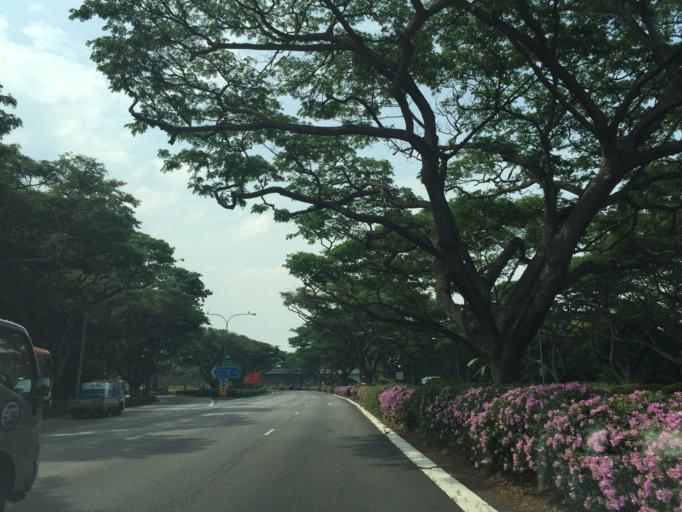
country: SG
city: Singapore
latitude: 1.3349
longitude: 103.9787
